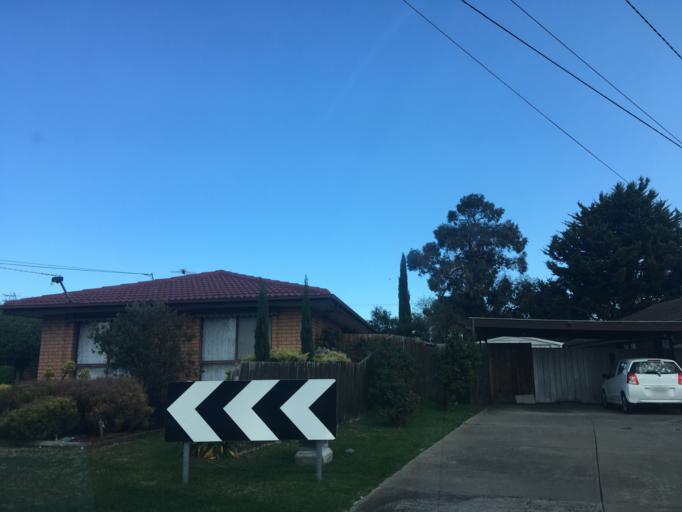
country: AU
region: Victoria
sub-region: Wyndham
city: Hoppers Crossing
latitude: -37.8701
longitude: 144.7039
